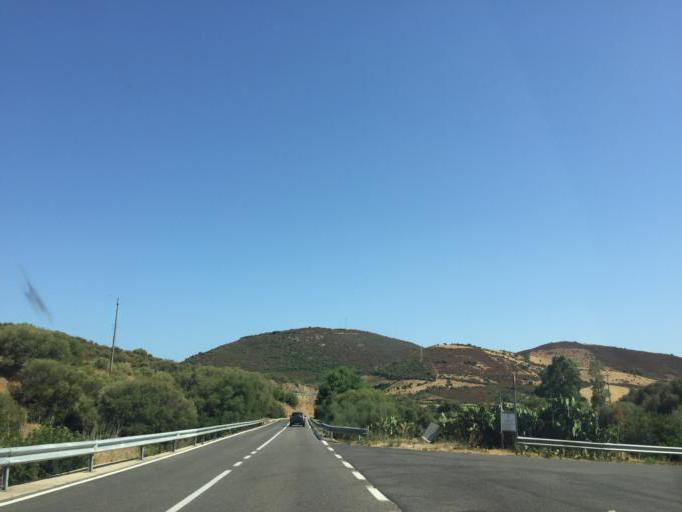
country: IT
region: Sardinia
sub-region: Provincia di Olbia-Tempio
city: San Teodoro
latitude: 40.7341
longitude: 9.6481
